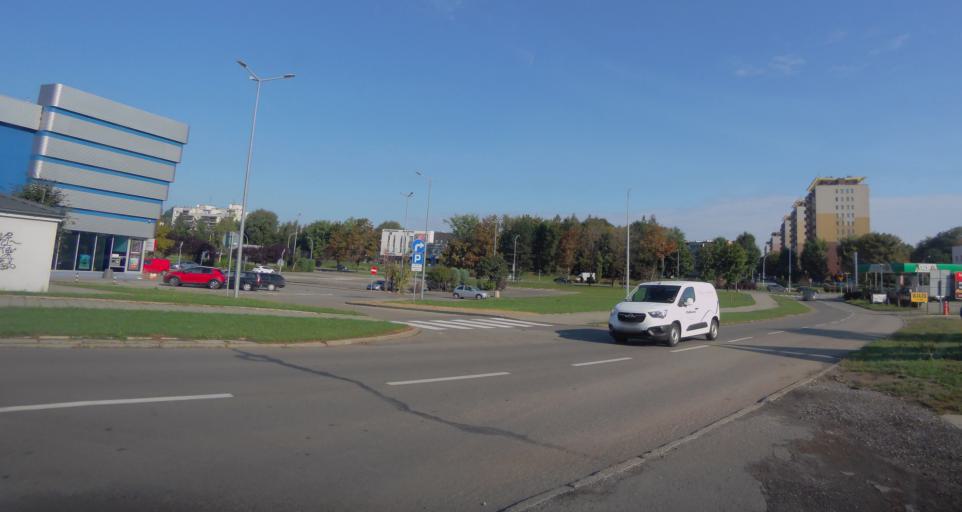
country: PL
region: Subcarpathian Voivodeship
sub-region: Rzeszow
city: Rzeszow
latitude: 50.0191
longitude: 21.9915
